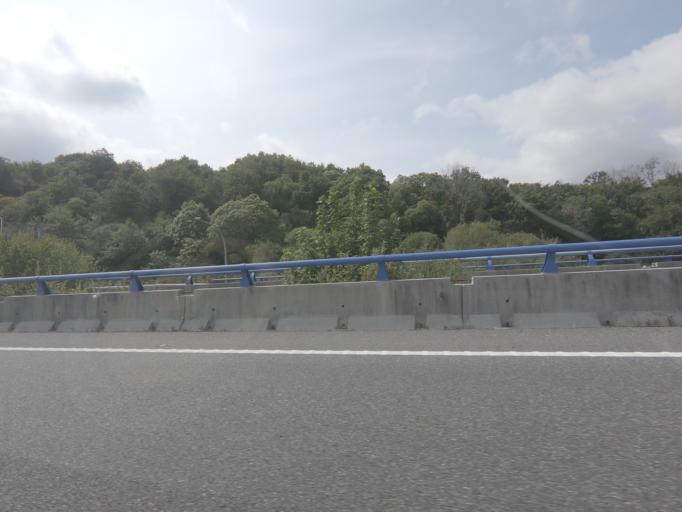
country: ES
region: Galicia
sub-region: Provincia de Pontevedra
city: Covelo
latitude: 42.1831
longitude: -8.3259
